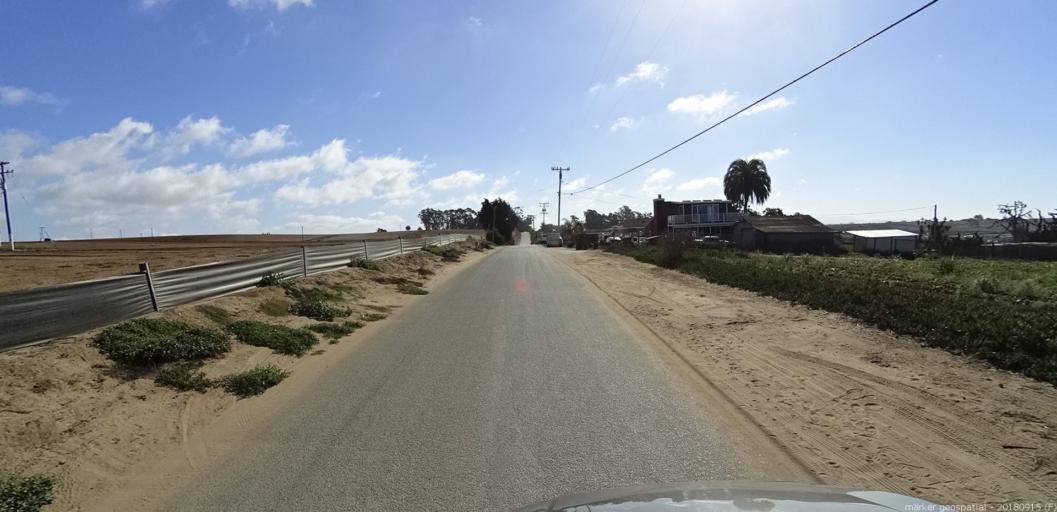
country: US
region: California
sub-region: Monterey County
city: Elkhorn
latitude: 36.8382
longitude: -121.7796
